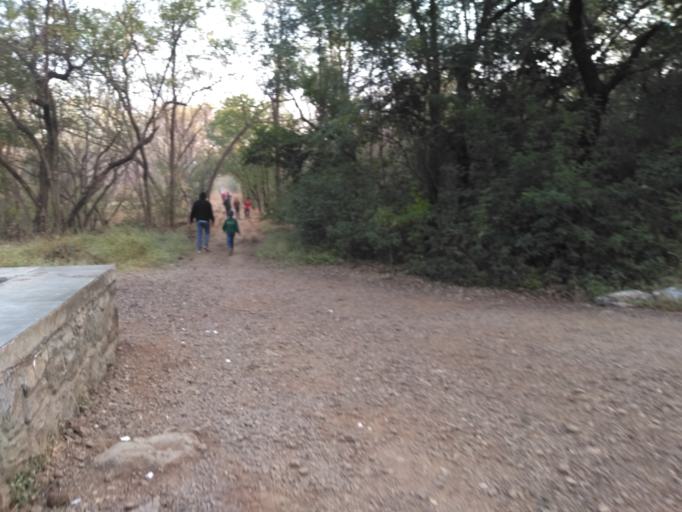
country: IN
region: Maharashtra
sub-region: Pune Division
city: Pune
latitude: 18.4705
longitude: 73.8397
